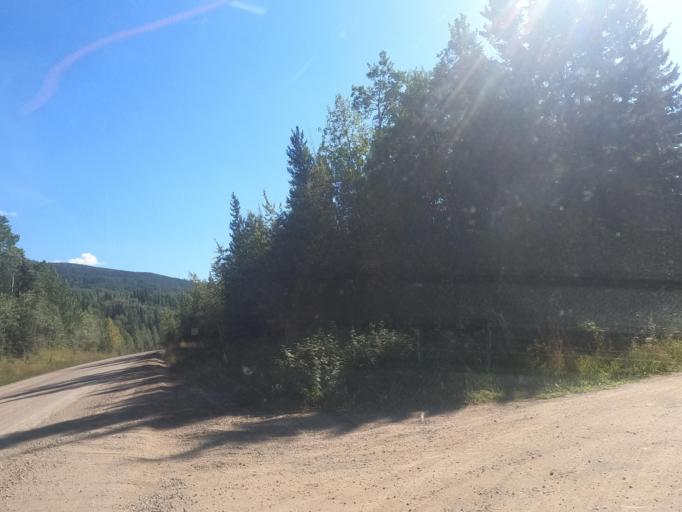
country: CA
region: British Columbia
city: Houston
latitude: 54.2869
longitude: -126.8498
